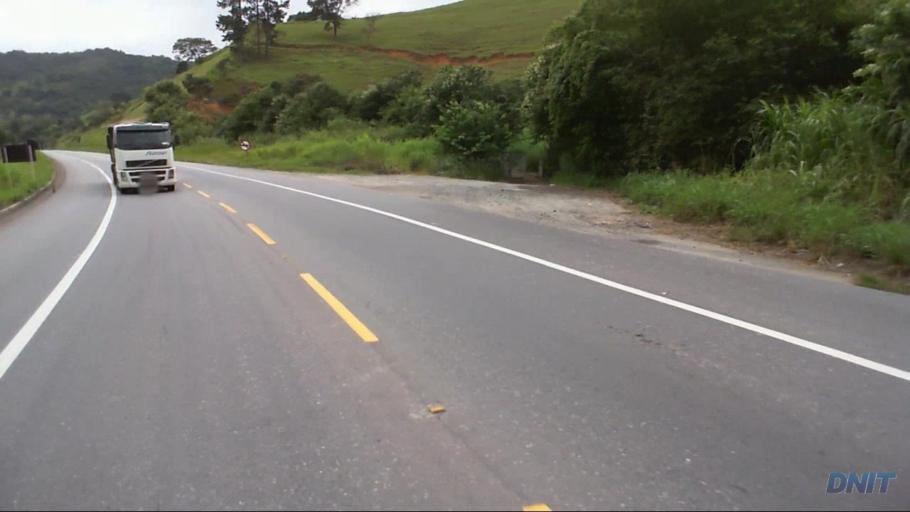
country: BR
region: Minas Gerais
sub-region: Nova Era
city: Nova Era
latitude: -19.7200
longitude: -43.0046
